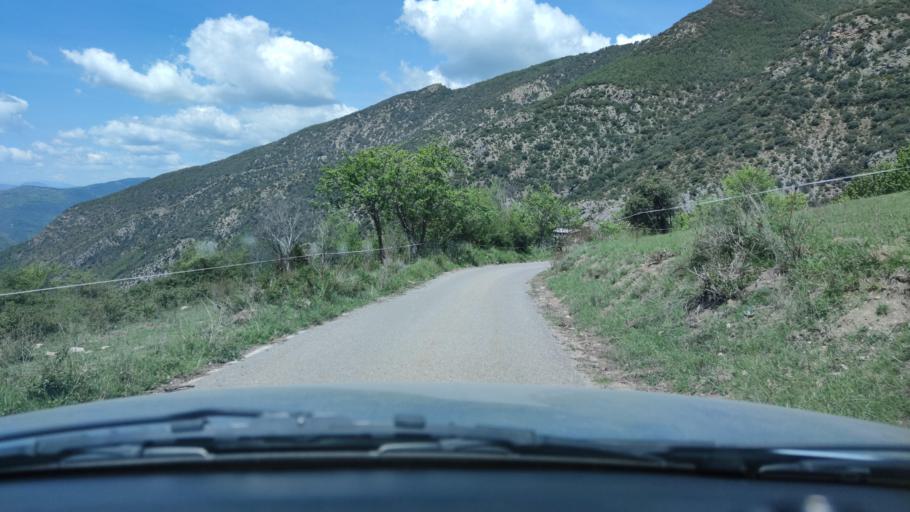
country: ES
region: Catalonia
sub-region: Provincia de Lleida
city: Sort
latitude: 42.3245
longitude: 1.1067
